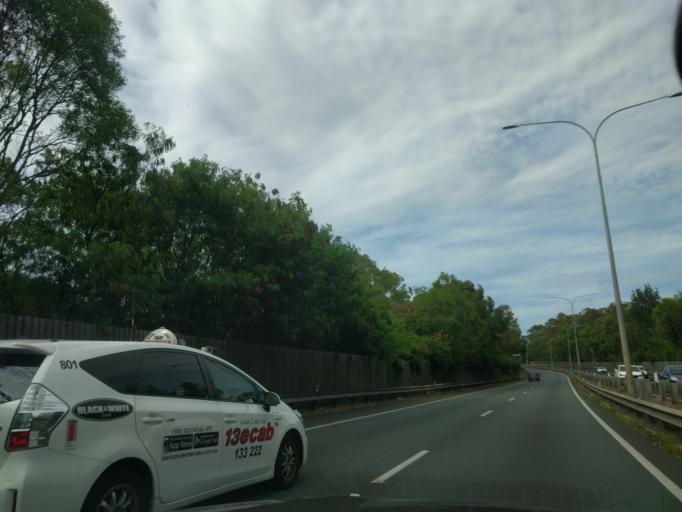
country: AU
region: Queensland
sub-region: Brisbane
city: Taringa
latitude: -27.5080
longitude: 152.9615
